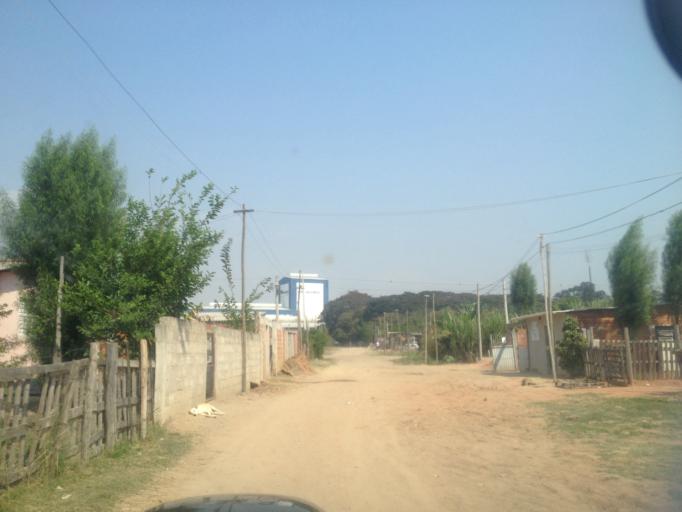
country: BR
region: Rio de Janeiro
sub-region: Porto Real
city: Porto Real
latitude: -22.4317
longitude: -44.3413
